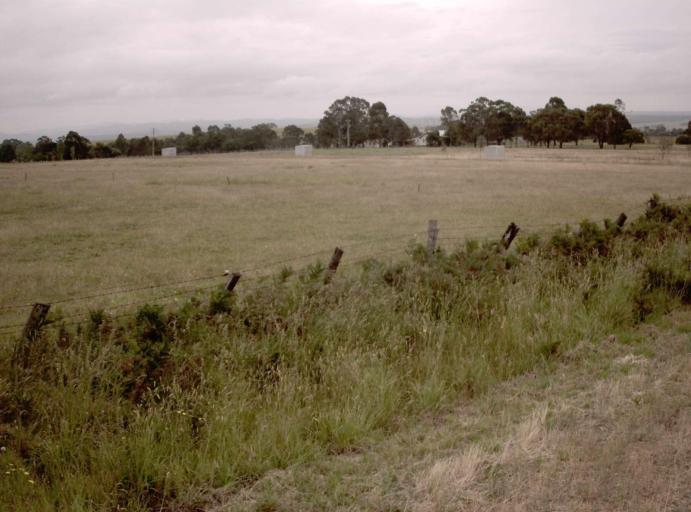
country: AU
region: Victoria
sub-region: East Gippsland
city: Bairnsdale
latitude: -37.8095
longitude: 147.4378
